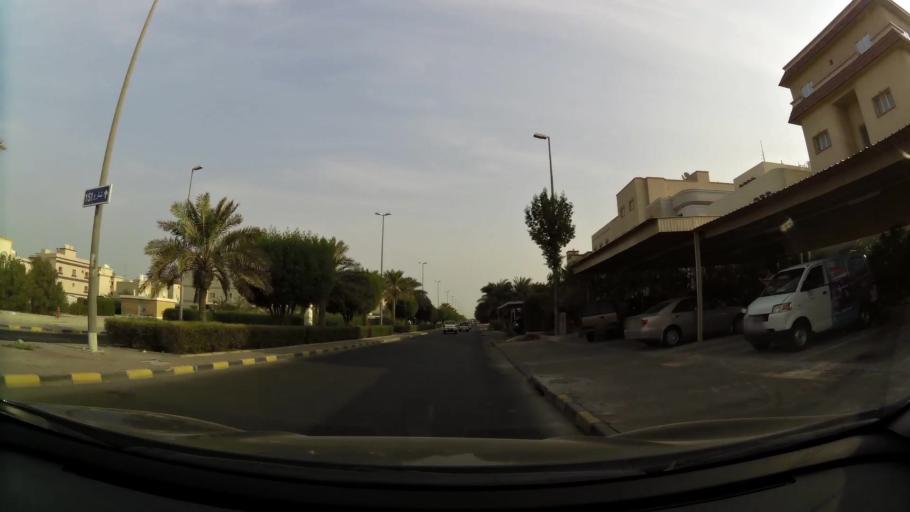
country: KW
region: Mubarak al Kabir
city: Mubarak al Kabir
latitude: 29.2163
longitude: 48.0632
